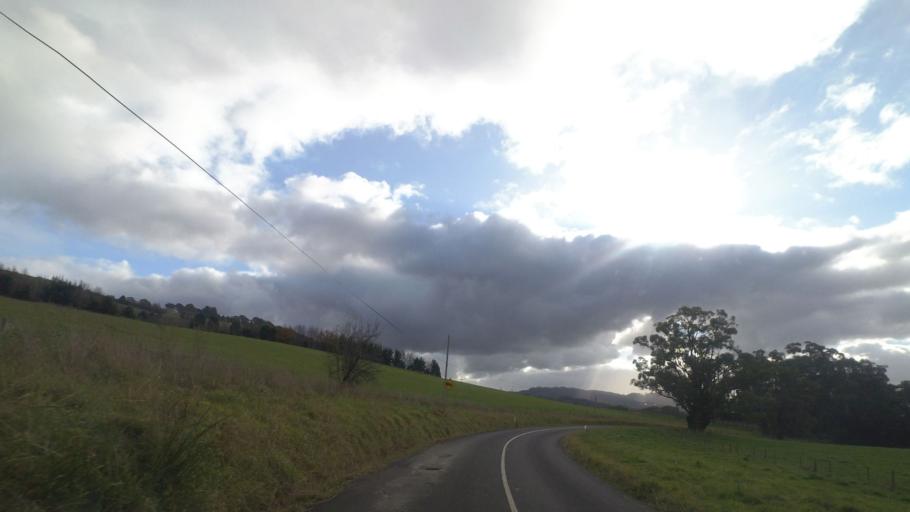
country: AU
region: Victoria
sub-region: Cardinia
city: Emerald
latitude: -37.9085
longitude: 145.4259
